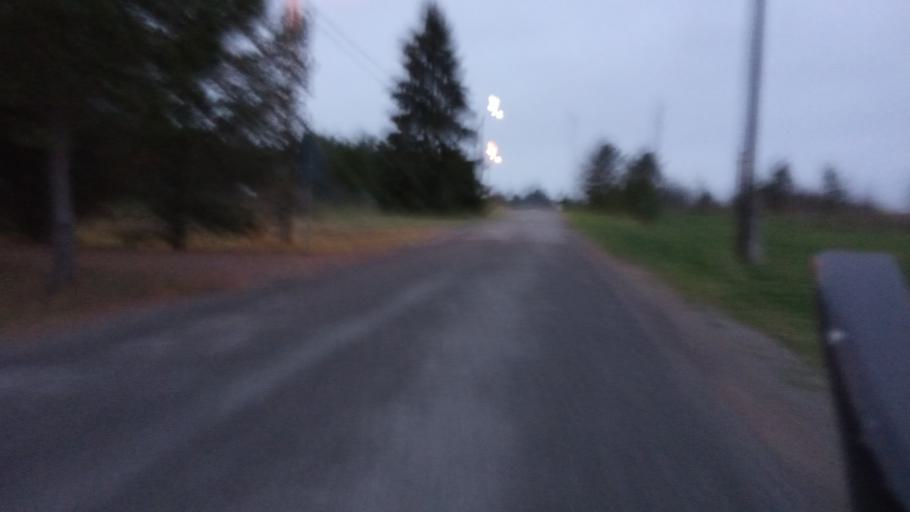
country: EE
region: Harju
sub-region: Kuusalu vald
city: Kuusalu
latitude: 59.4502
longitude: 25.4258
